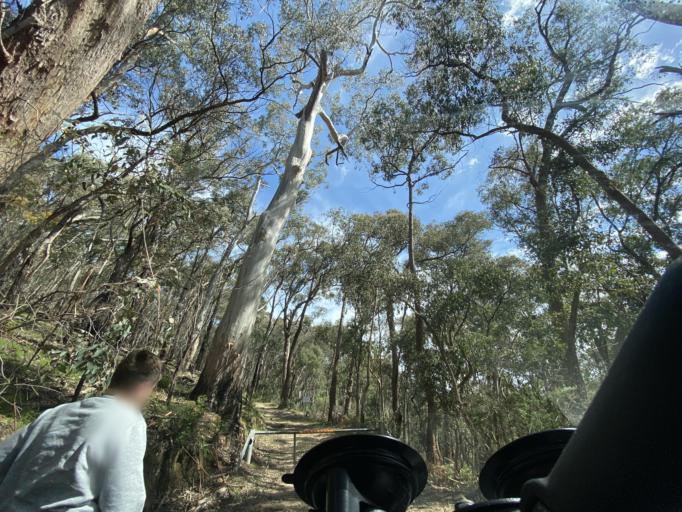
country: AU
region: Victoria
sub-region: Mansfield
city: Mansfield
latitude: -36.8340
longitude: 146.1005
